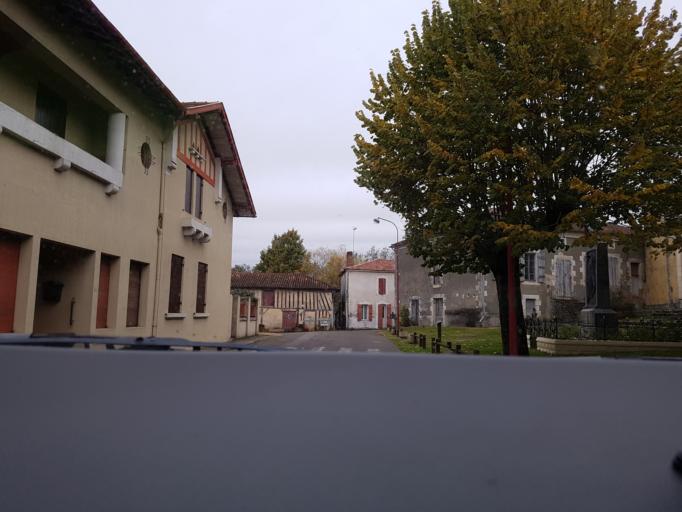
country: FR
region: Aquitaine
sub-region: Departement des Landes
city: Roquefort
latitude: 44.1000
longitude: -0.4057
